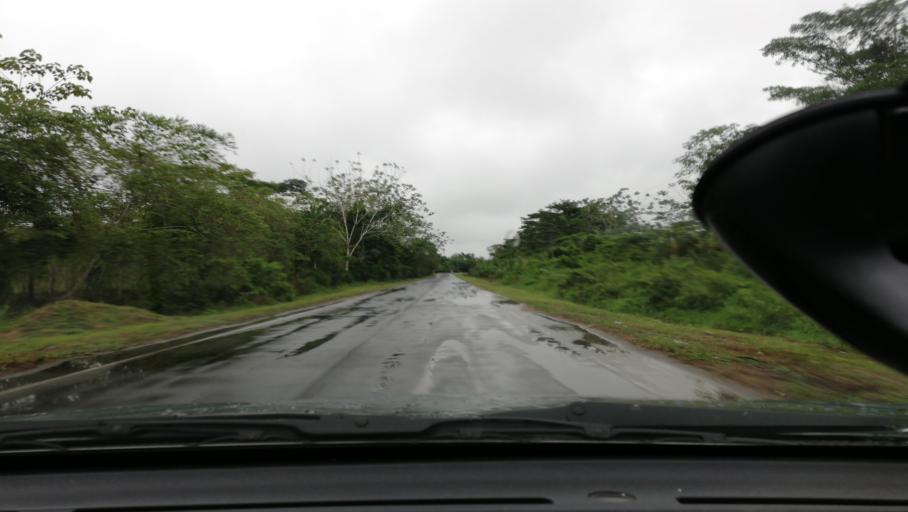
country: PE
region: Loreto
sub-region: Provincia de Maynas
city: San Juan
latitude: -4.0388
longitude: -73.4367
